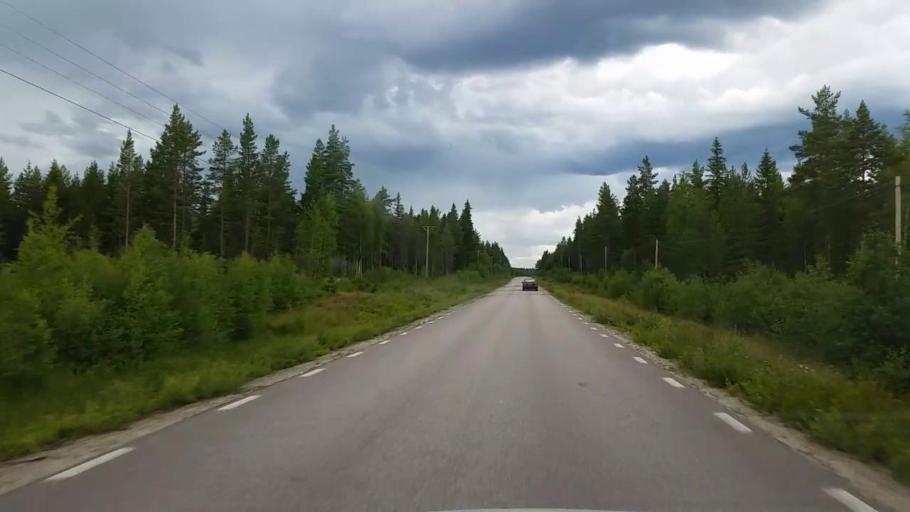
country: SE
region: Gaevleborg
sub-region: Ovanakers Kommun
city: Edsbyn
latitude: 61.4625
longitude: 15.8725
